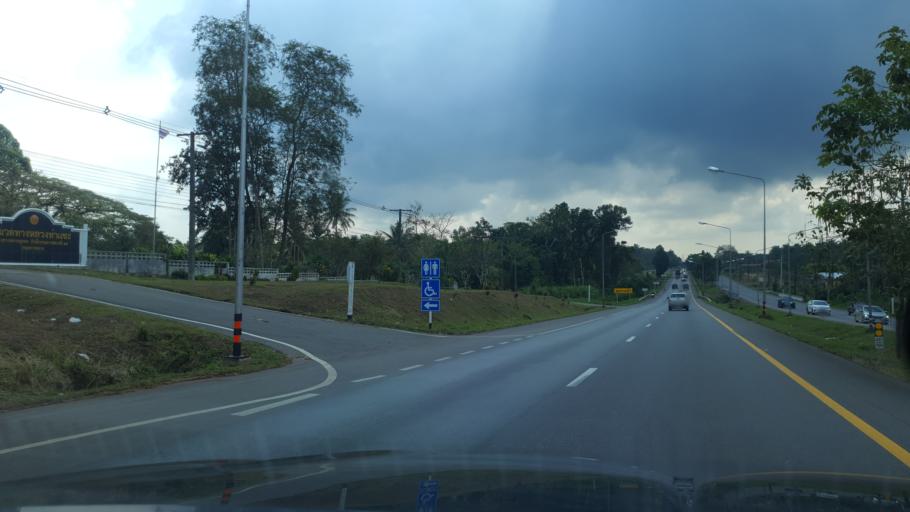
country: TH
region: Chumphon
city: Tha Sae
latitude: 10.7577
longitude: 99.2008
